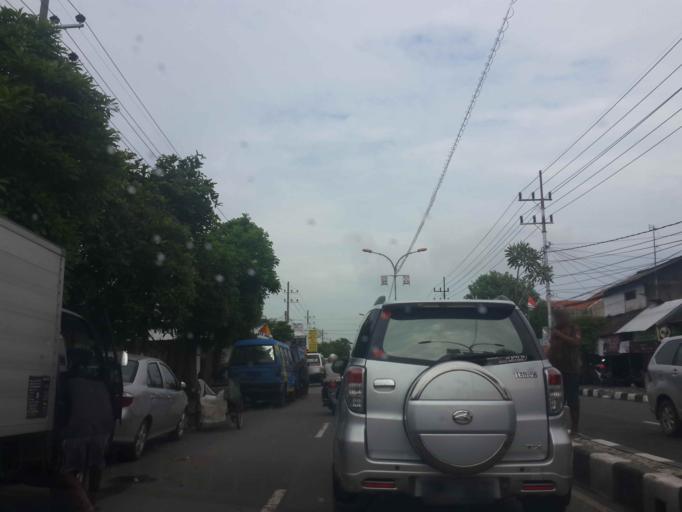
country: ID
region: East Java
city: Kebomas
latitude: -7.1651
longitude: 112.6373
